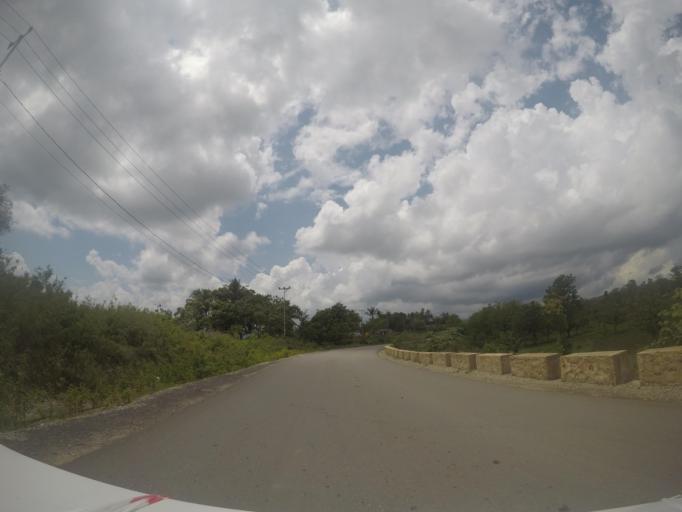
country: TL
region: Baucau
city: Venilale
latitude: -8.5602
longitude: 126.4014
